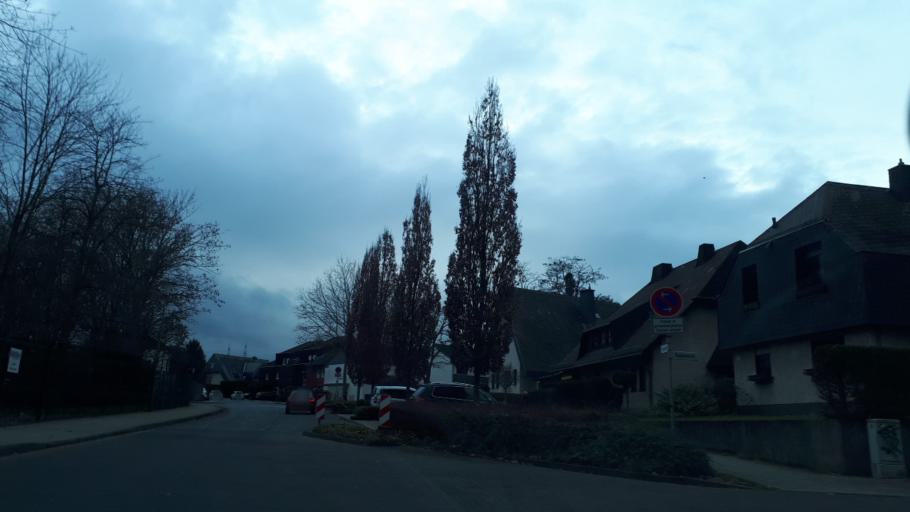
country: DE
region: Rheinland-Pfalz
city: Andernach
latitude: 50.4290
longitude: 7.3952
